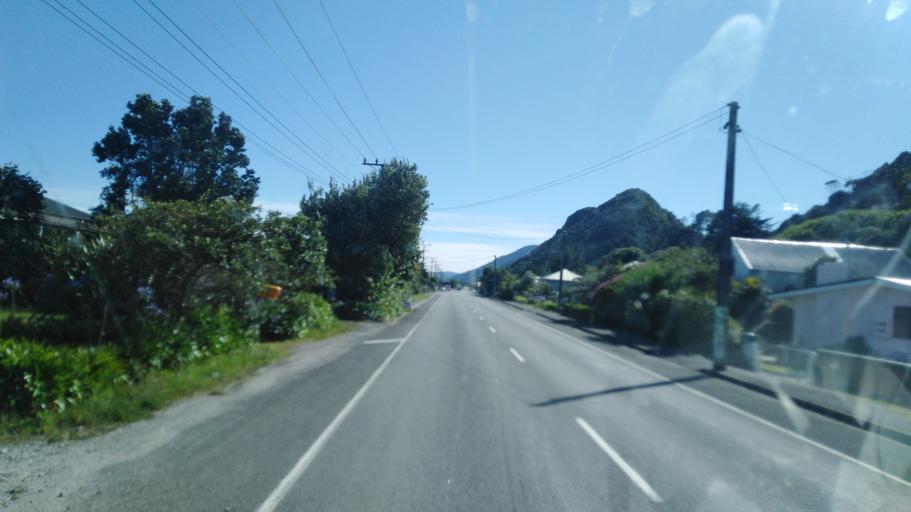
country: NZ
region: West Coast
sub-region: Buller District
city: Westport
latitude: -41.6312
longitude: 171.8525
